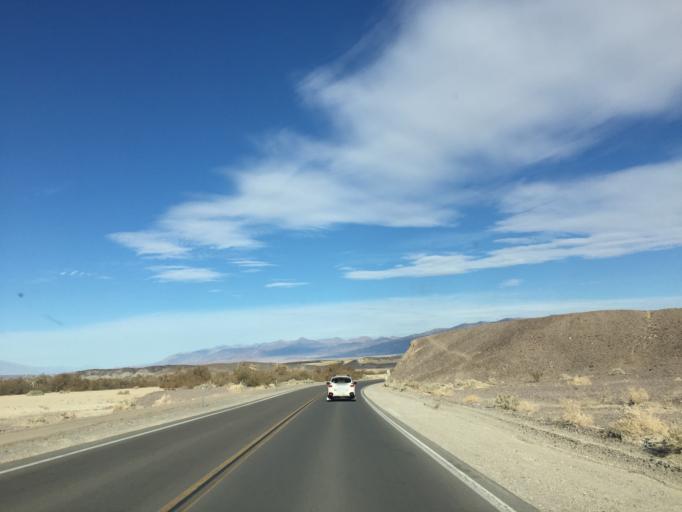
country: US
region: Nevada
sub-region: Nye County
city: Beatty
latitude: 36.4672
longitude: -116.8666
